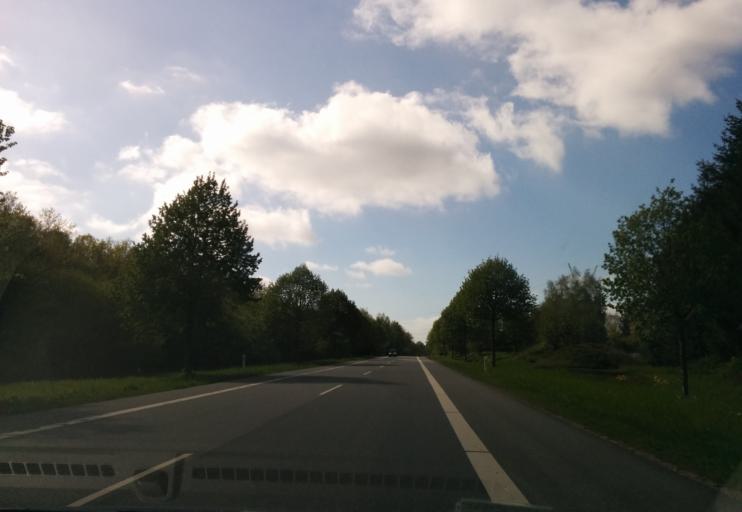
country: DK
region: South Denmark
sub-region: Assens Kommune
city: Arup
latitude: 55.4075
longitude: 10.0755
